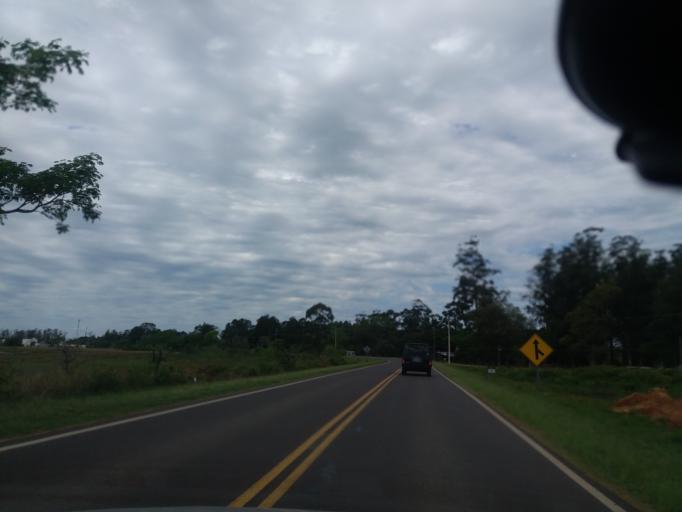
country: AR
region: Corrientes
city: Corrientes
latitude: -27.4539
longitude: -58.7213
